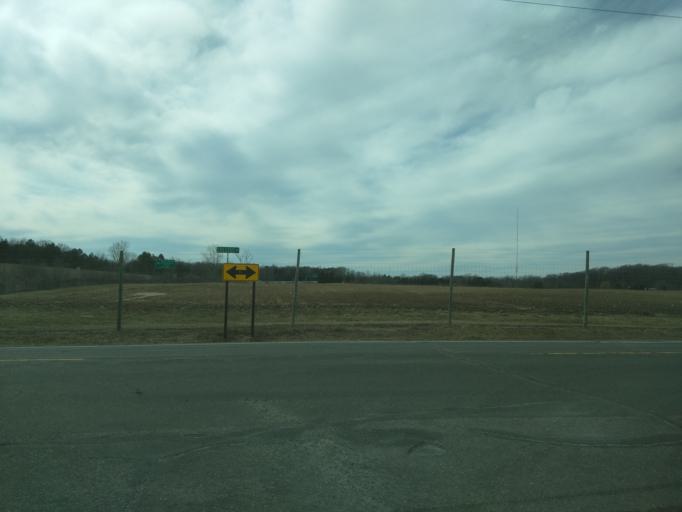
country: US
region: Michigan
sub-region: Ingham County
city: Holt
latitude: 42.6700
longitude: -84.4839
